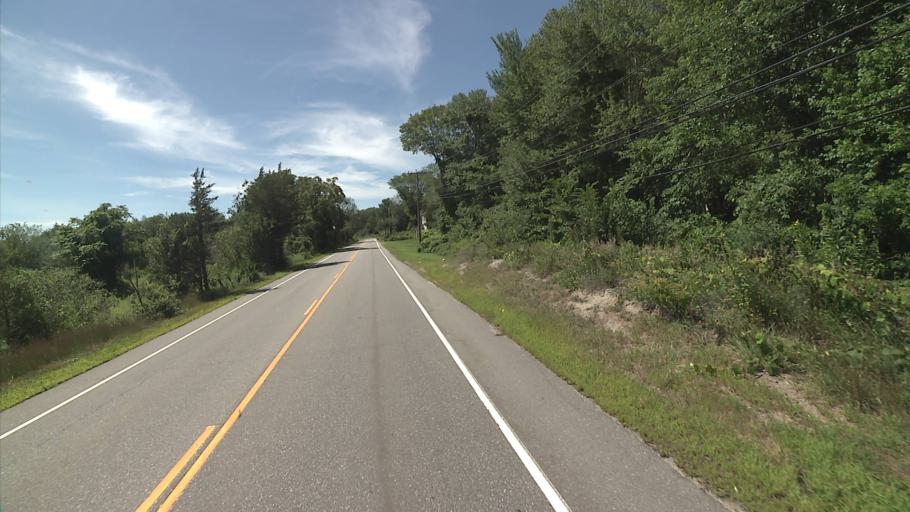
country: US
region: Connecticut
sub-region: Windham County
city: Killingly Center
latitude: 41.8403
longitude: -71.8573
